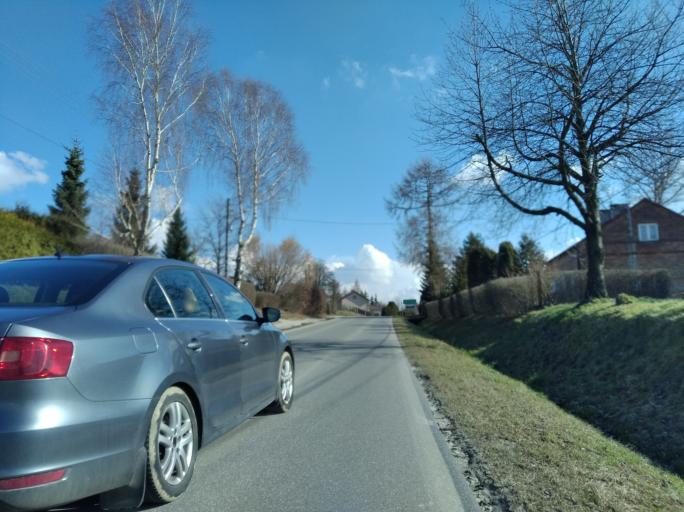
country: PL
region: Subcarpathian Voivodeship
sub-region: Powiat strzyzowski
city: Frysztak
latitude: 49.8432
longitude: 21.5861
